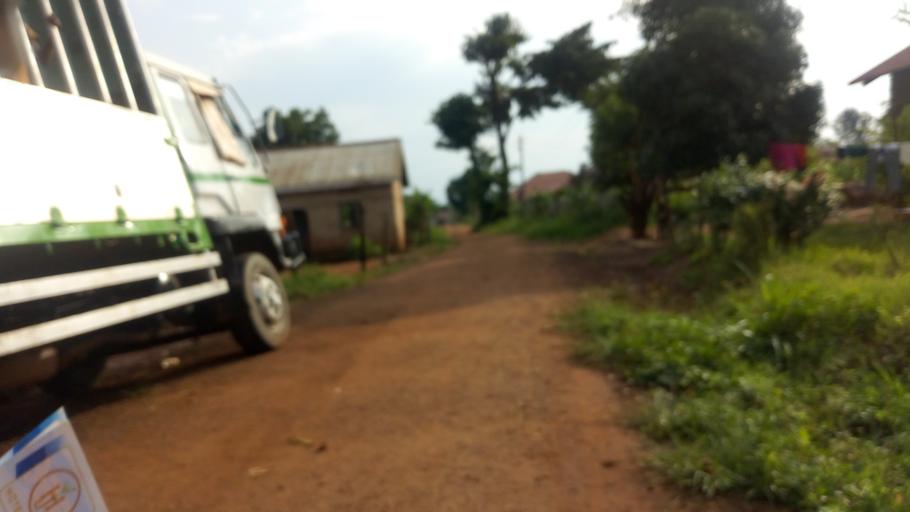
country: UG
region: Western Region
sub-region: Kiryandongo District
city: Kiryandongo
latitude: 1.8041
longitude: 32.0077
